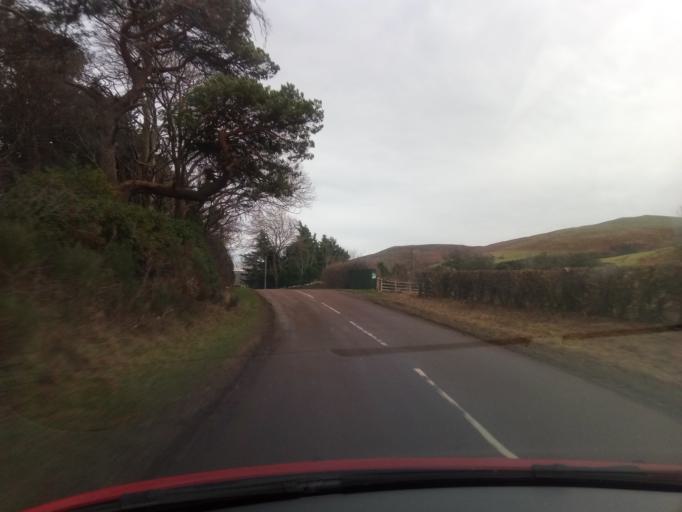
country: GB
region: England
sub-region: Northumberland
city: Kirknewton
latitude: 55.5664
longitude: -2.1037
